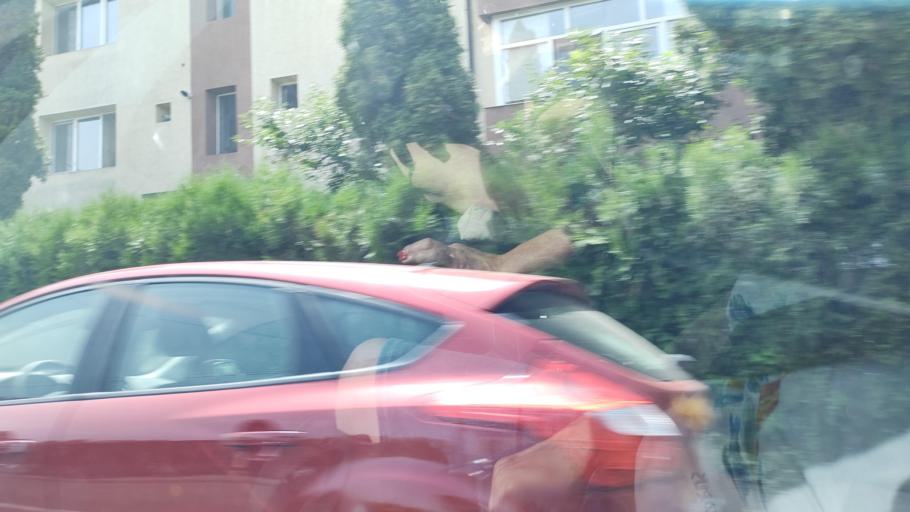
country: RO
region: Mehedinti
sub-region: Municipiul Drobeta-Turnu Severin
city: Drobeta-Turnu Severin
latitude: 44.6246
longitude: 22.6638
